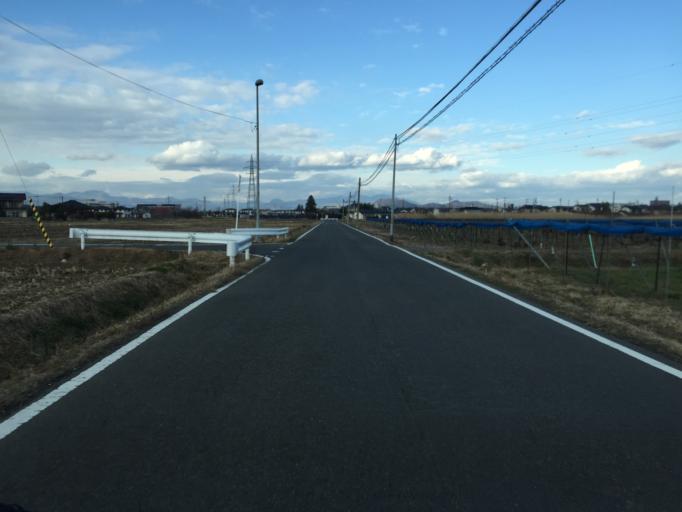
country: JP
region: Fukushima
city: Fukushima-shi
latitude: 37.7142
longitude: 140.4484
